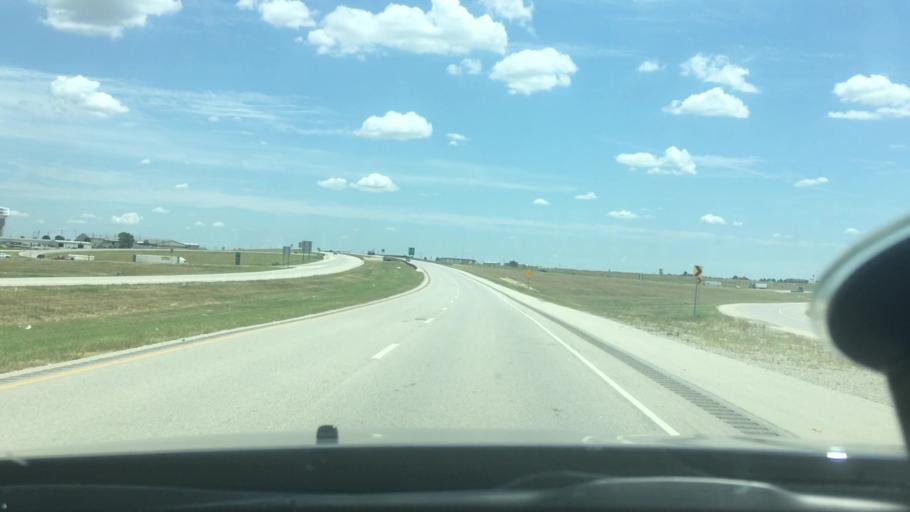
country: US
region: Oklahoma
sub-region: Bryan County
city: Calera
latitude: 33.9716
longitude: -96.4204
